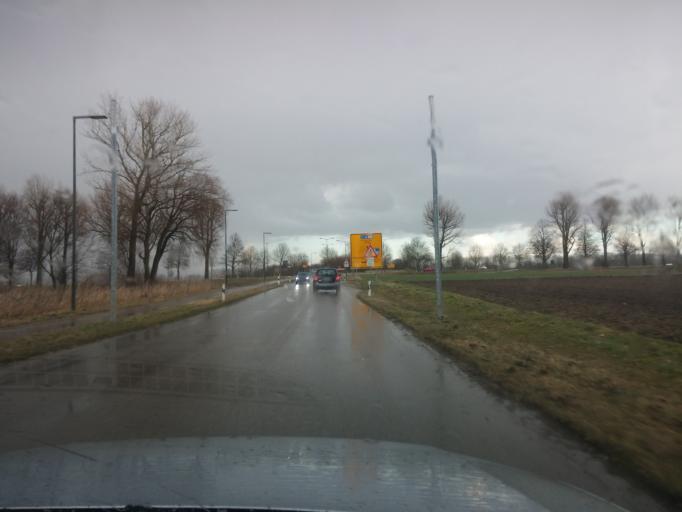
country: DE
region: Bavaria
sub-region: Upper Bavaria
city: Ismaning
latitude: 48.2191
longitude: 11.6859
